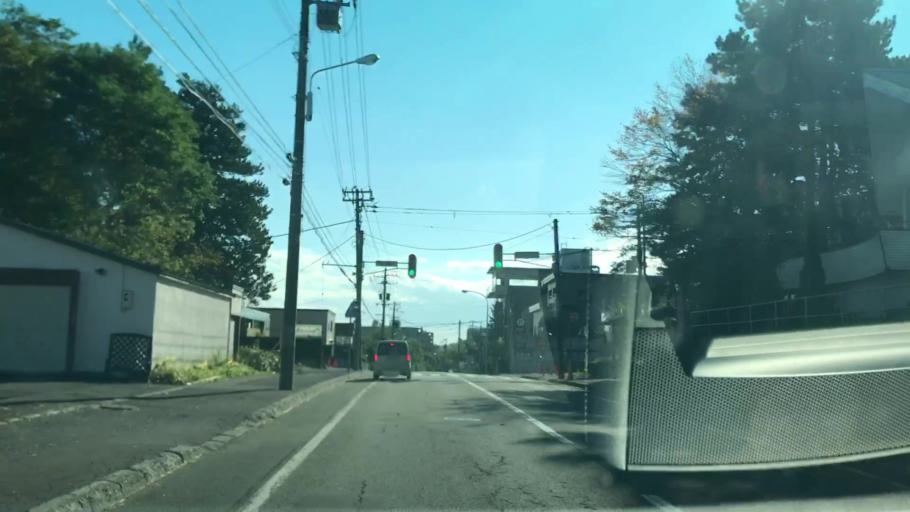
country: JP
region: Hokkaido
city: Sapporo
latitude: 43.0370
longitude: 141.3262
